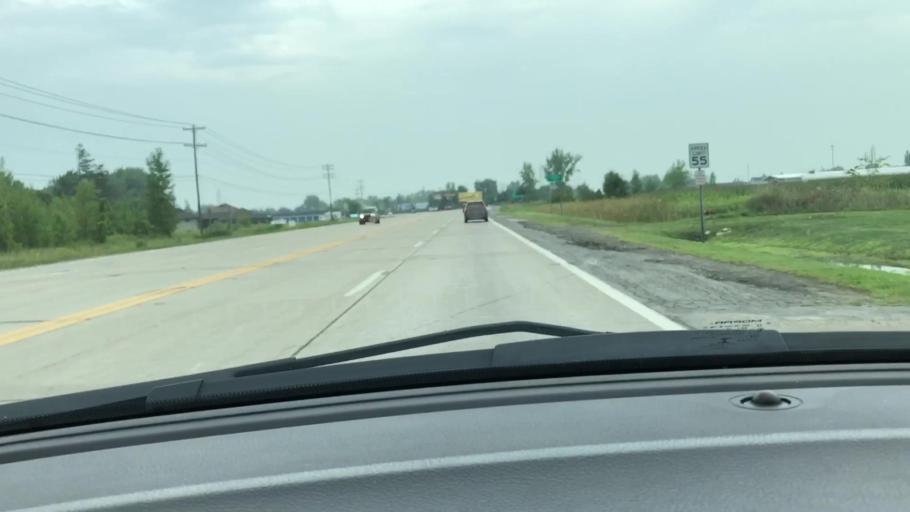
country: US
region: Michigan
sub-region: Saginaw County
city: Freeland
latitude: 43.4821
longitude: -84.0913
